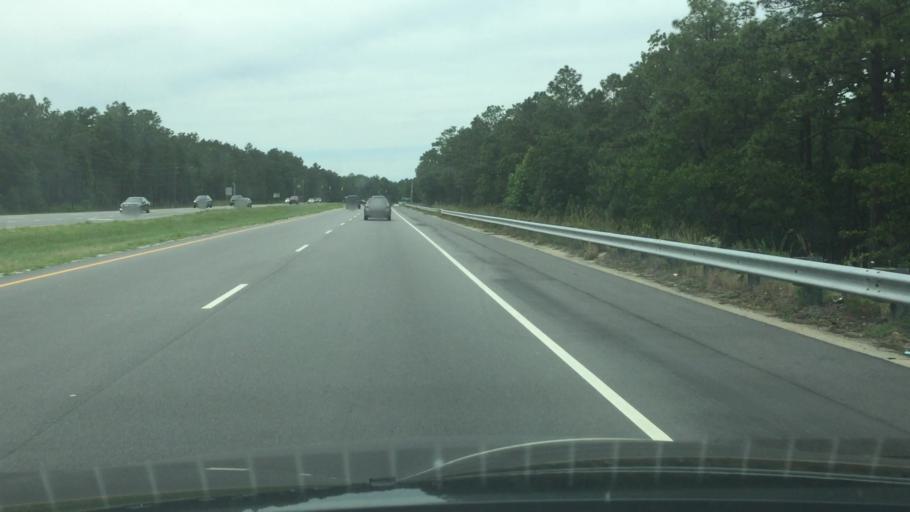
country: US
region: North Carolina
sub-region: Cumberland County
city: Spring Lake
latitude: 35.2288
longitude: -79.0131
